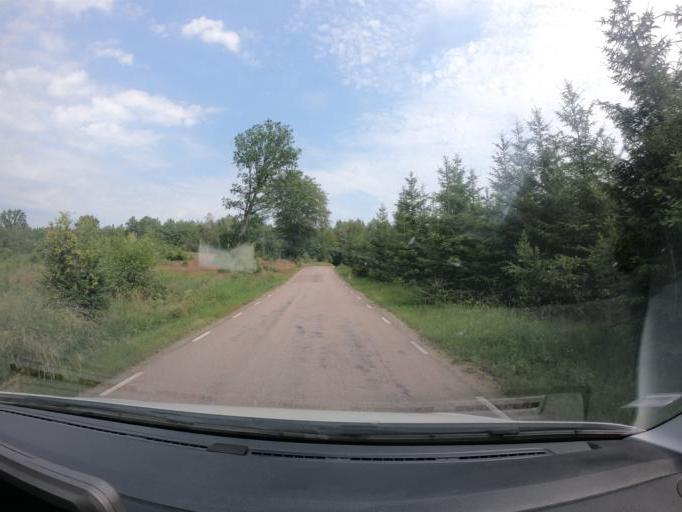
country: SE
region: Skane
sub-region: Hassleholms Kommun
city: Bjarnum
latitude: 56.2569
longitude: 13.7015
